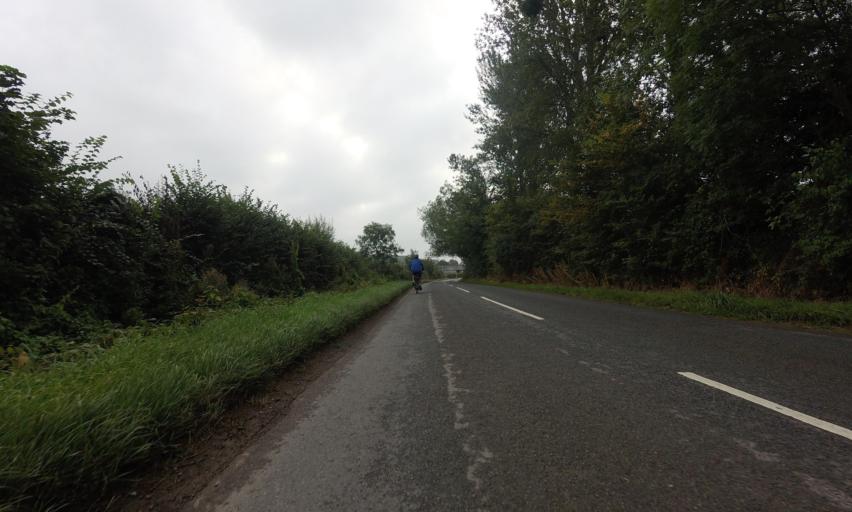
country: GB
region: England
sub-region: Gloucestershire
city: Gotherington
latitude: 51.9671
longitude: -2.0240
